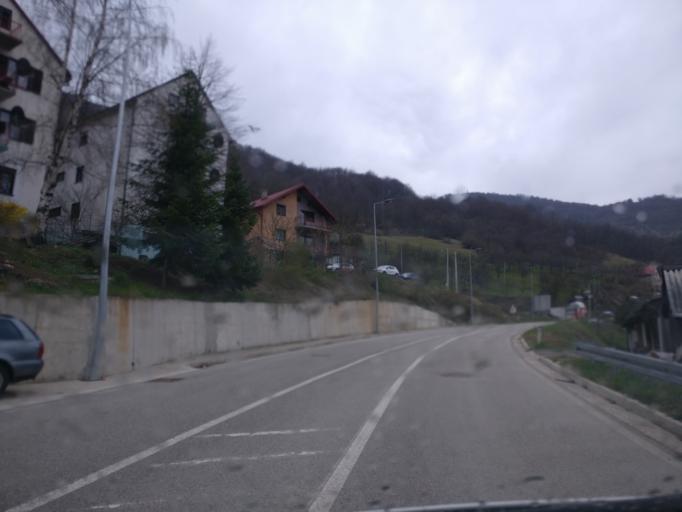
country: ME
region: Opstina Pluzine
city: Pluzine
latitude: 43.1559
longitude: 18.8466
